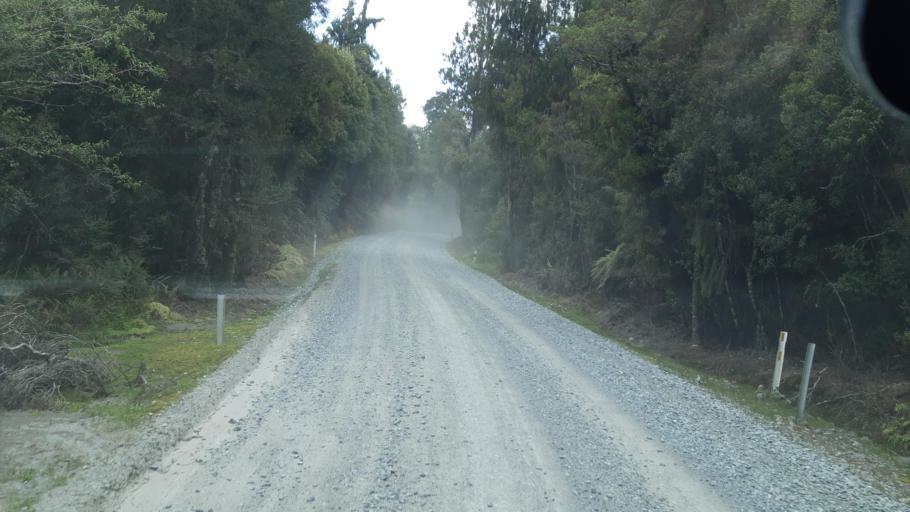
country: NZ
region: West Coast
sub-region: Grey District
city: Greymouth
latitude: -42.7241
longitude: 171.2379
